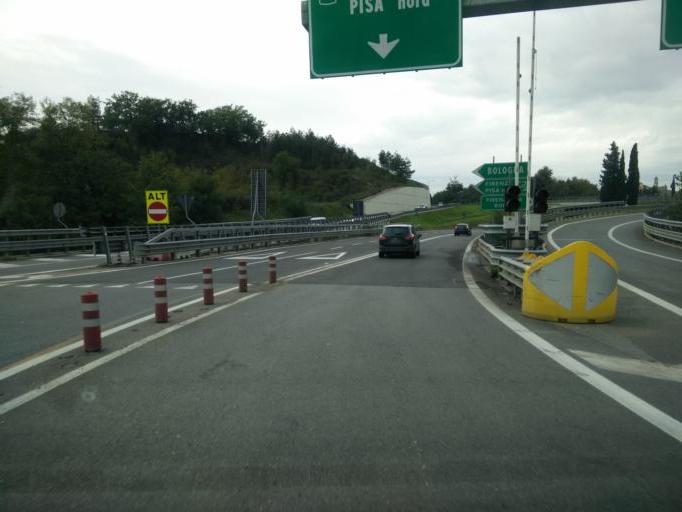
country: IT
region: Tuscany
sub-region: Province of Florence
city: Tavarnuzze
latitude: 43.7219
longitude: 11.2223
